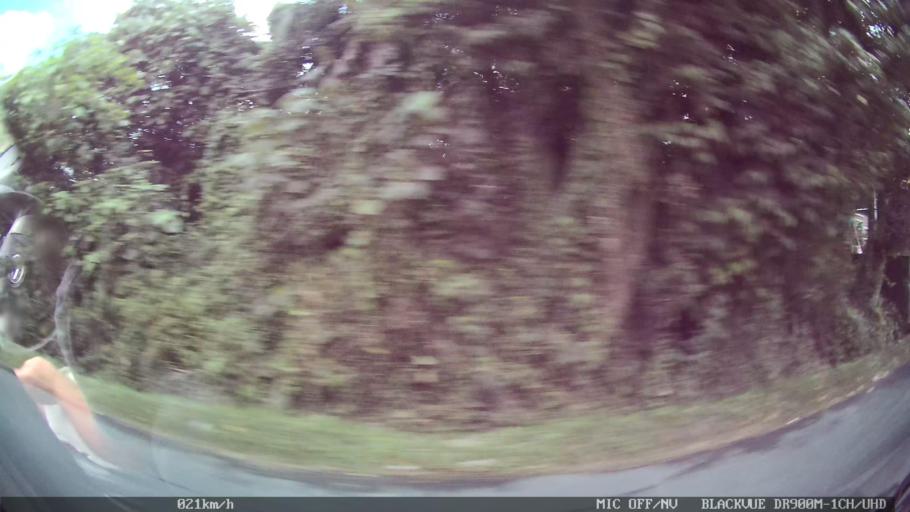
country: ID
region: Bali
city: Banjar Desa
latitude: -8.5741
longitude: 115.2867
